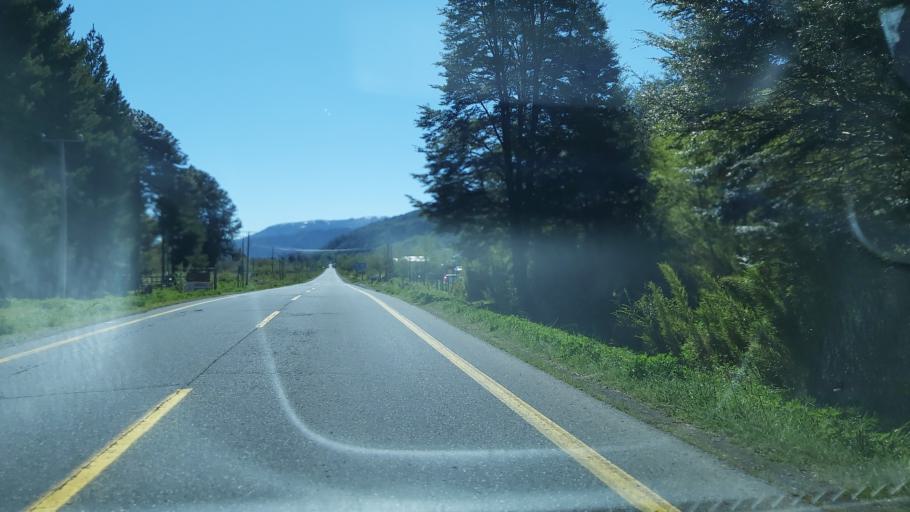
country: CL
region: Araucania
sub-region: Provincia de Cautin
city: Vilcun
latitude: -38.4777
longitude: -71.5396
